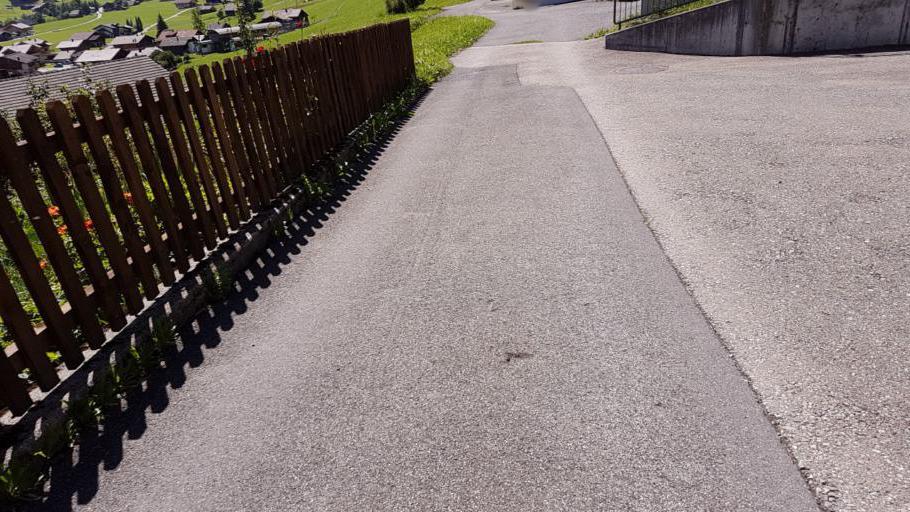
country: CH
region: Bern
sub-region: Frutigen-Niedersimmental District
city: Adelboden
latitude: 46.4838
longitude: 7.5558
